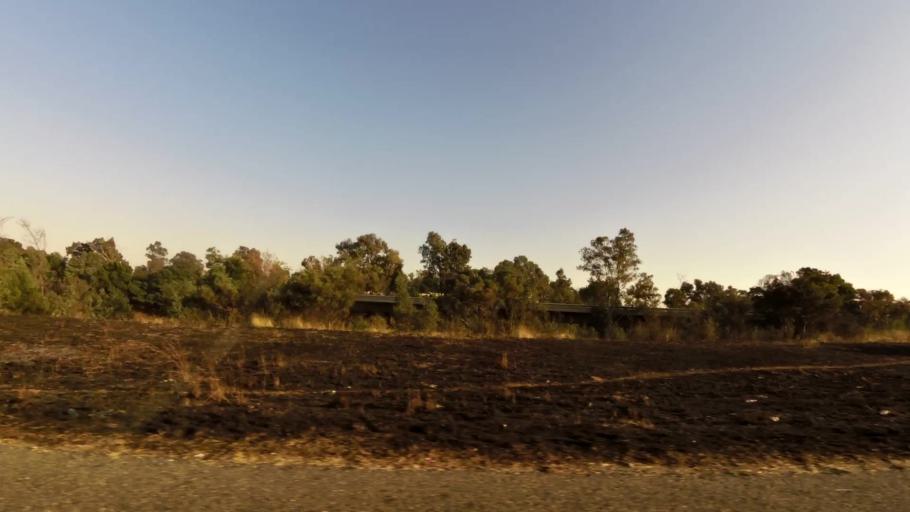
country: ZA
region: Gauteng
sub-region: City of Johannesburg Metropolitan Municipality
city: Johannesburg
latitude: -26.2596
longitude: 27.9832
